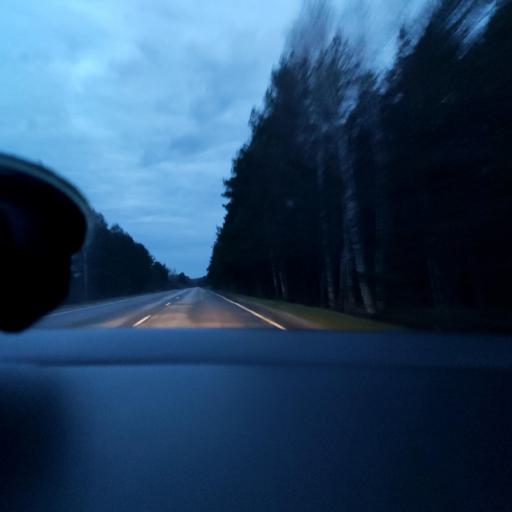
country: RU
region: Moskovskaya
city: Shaturtorf
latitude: 55.4285
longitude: 39.3417
